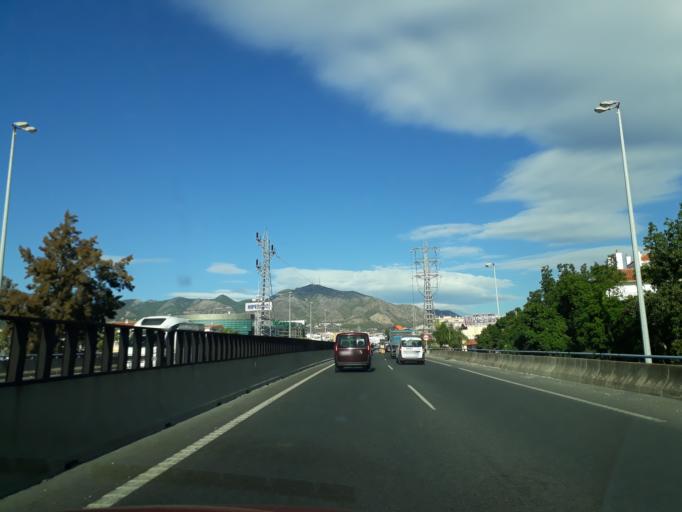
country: ES
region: Andalusia
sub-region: Provincia de Malaga
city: Fuengirola
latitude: 36.5450
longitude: -4.6335
